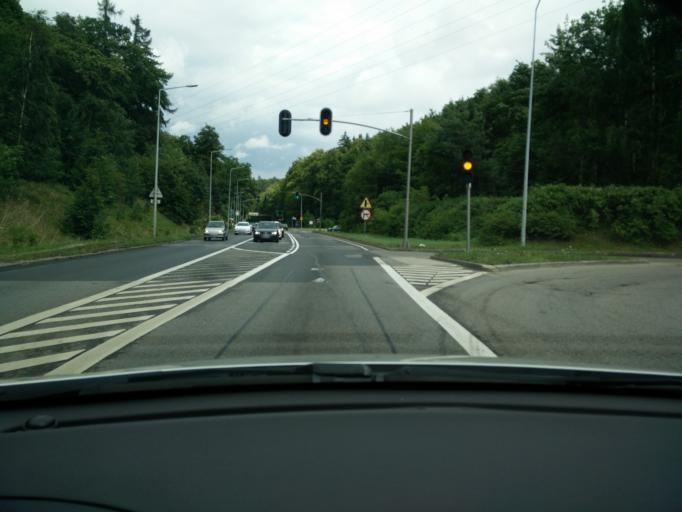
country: PL
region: Pomeranian Voivodeship
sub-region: Gdynia
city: Wielki Kack
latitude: 54.4288
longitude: 18.4930
